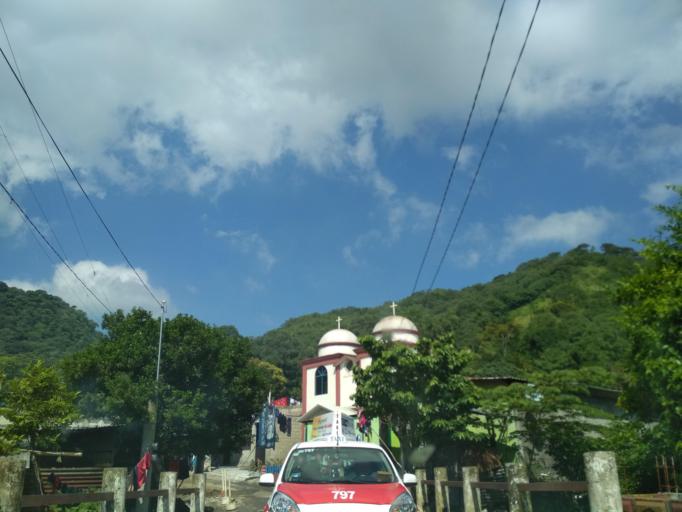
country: MX
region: Veracruz
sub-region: San Andres Tuxtla
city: Texcaltitan Xoteapan (Texcaltitan)
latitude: 18.4482
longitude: -95.2533
